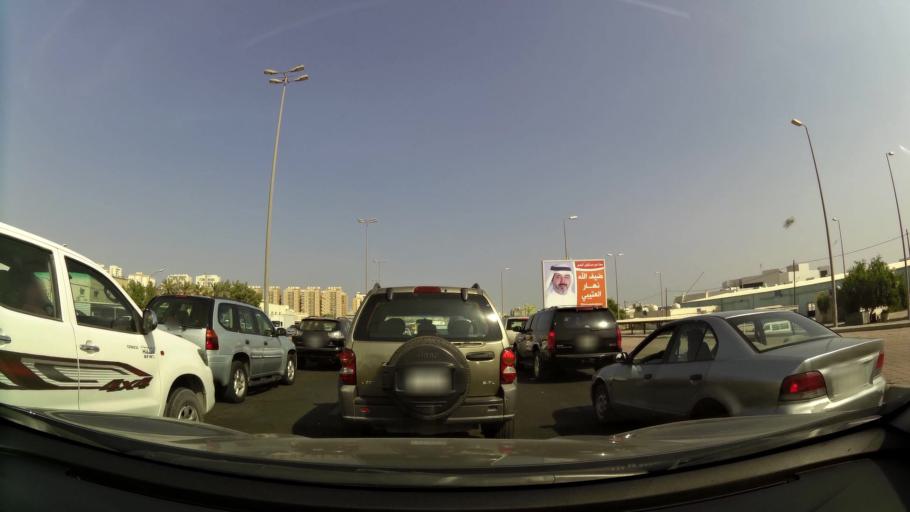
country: KW
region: Al Ahmadi
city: Ar Riqqah
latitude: 29.1357
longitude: 48.1112
